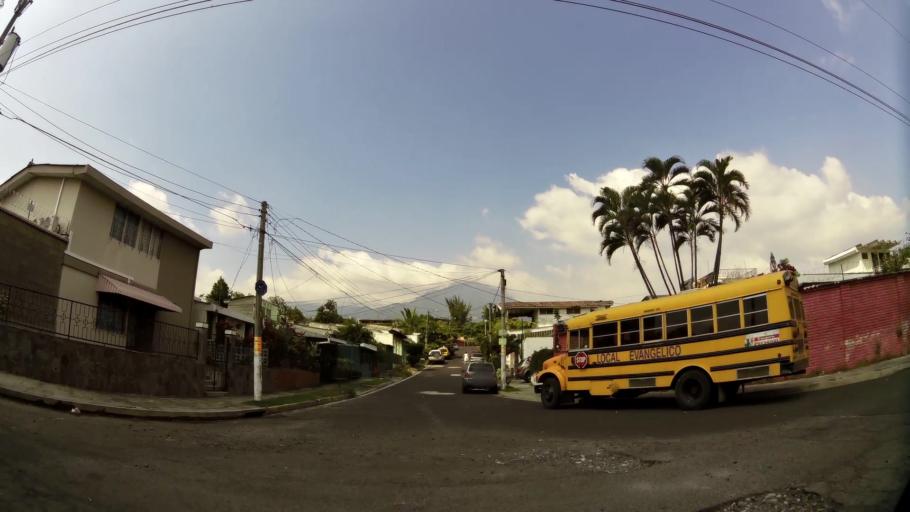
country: SV
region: San Salvador
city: Mejicanos
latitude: 13.7106
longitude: -89.2168
